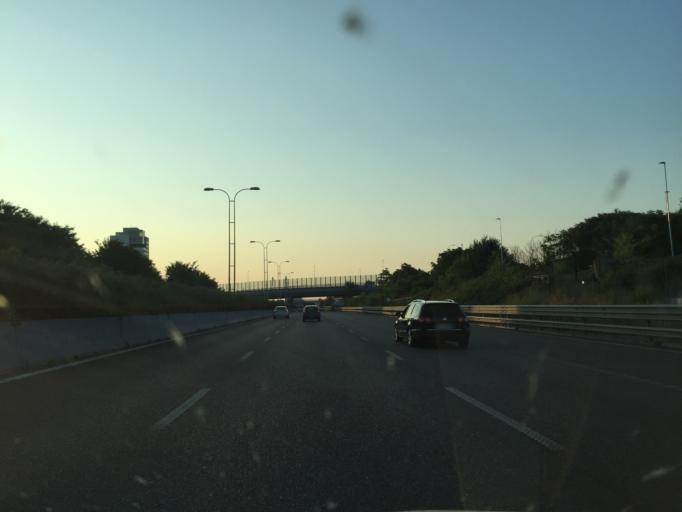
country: IT
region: Lombardy
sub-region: Provincia di Brescia
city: Brescia
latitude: 45.5211
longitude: 10.1894
